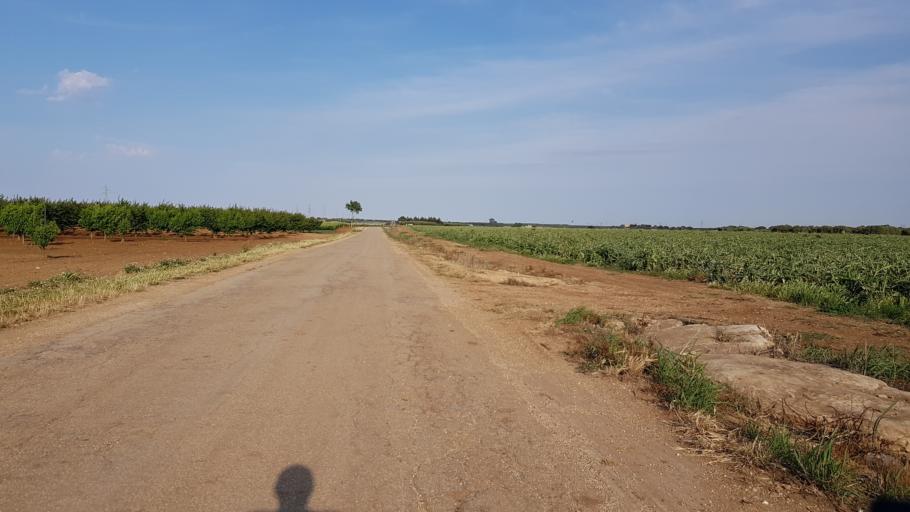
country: IT
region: Apulia
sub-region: Provincia di Brindisi
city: Mesagne
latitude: 40.6215
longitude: 17.8052
